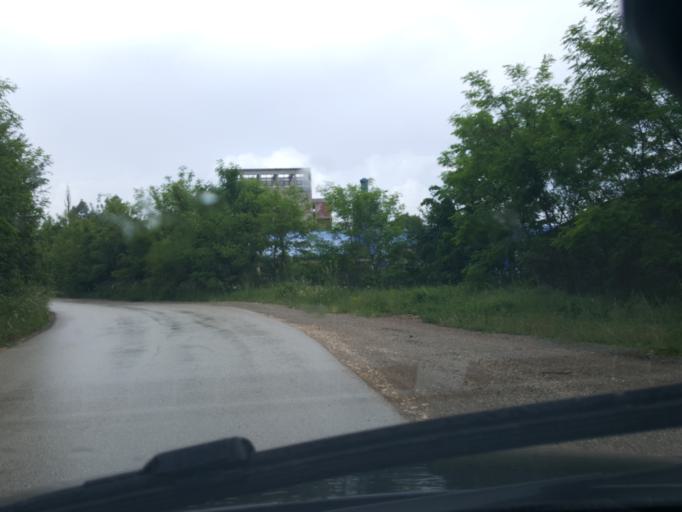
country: RS
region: Central Serbia
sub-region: Zajecarski Okrug
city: Boljevac
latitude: 43.8016
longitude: 21.8978
